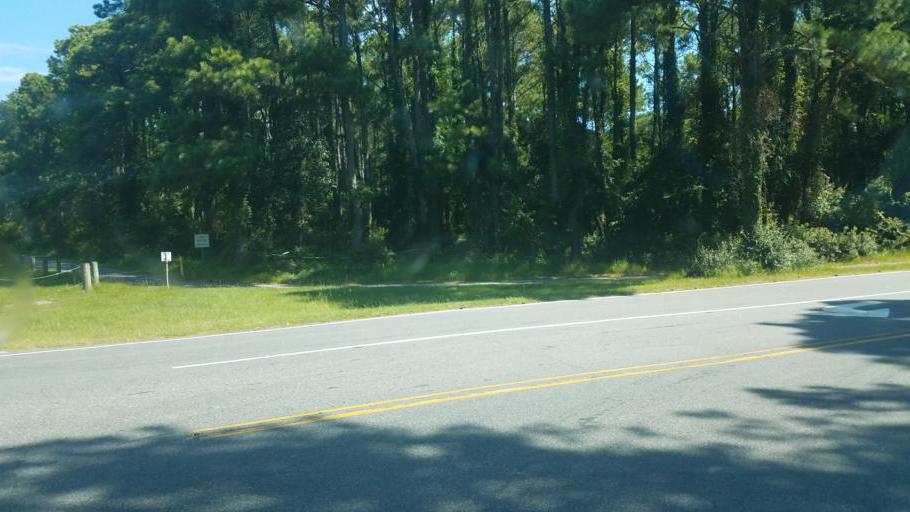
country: US
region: North Carolina
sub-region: Dare County
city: Kill Devil Hills
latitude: 36.0133
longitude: -75.6771
